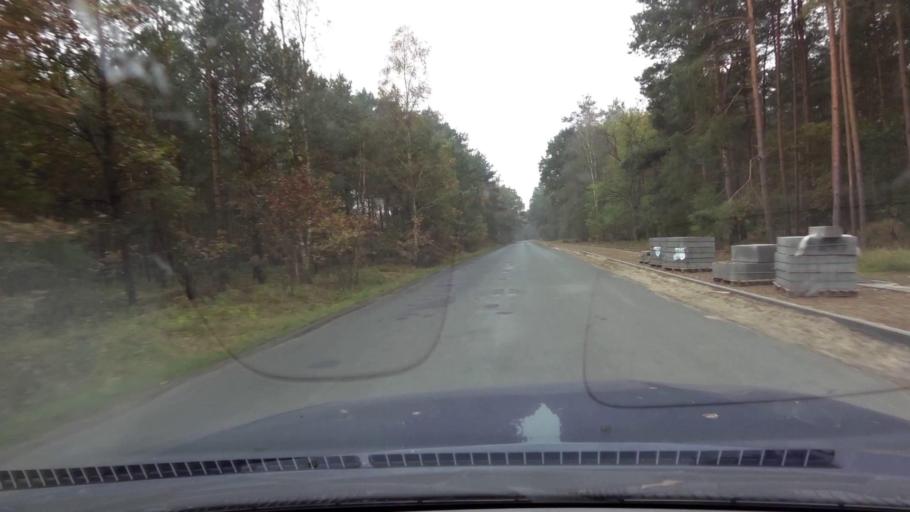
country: PL
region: West Pomeranian Voivodeship
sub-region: Powiat goleniowski
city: Goleniow
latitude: 53.5348
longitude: 14.7618
